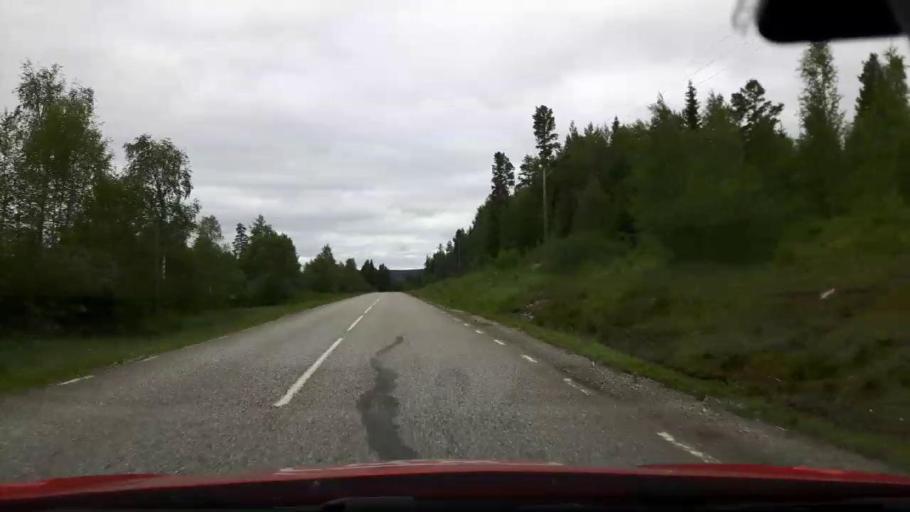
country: SE
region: Jaemtland
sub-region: Stroemsunds Kommun
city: Stroemsund
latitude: 63.3160
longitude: 15.7627
